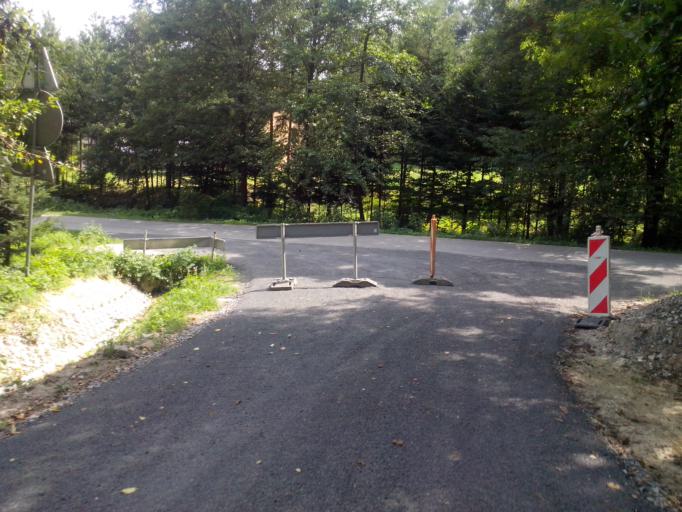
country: PL
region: Subcarpathian Voivodeship
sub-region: Powiat strzyzowski
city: Strzyzow
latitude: 49.7989
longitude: 21.8170
